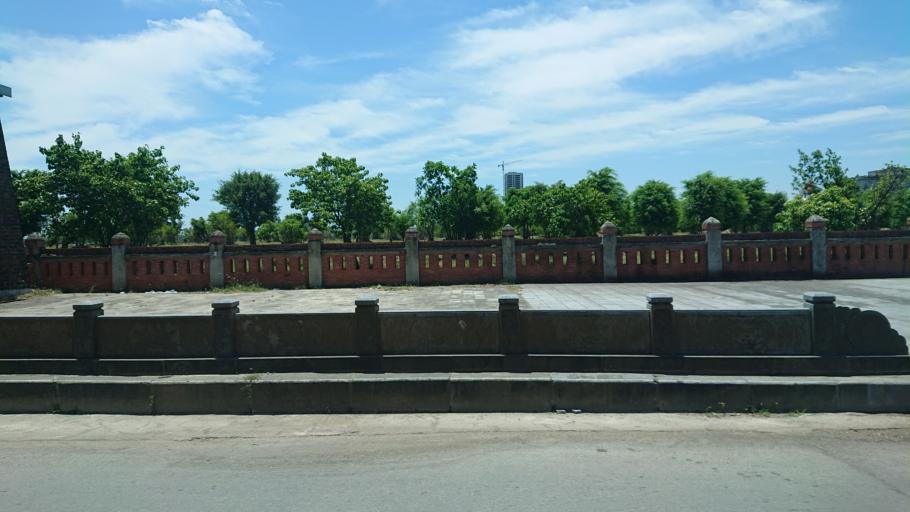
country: VN
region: Ninh Binh
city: Thanh Pho Ninh Binh
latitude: 20.2627
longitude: 105.9606
